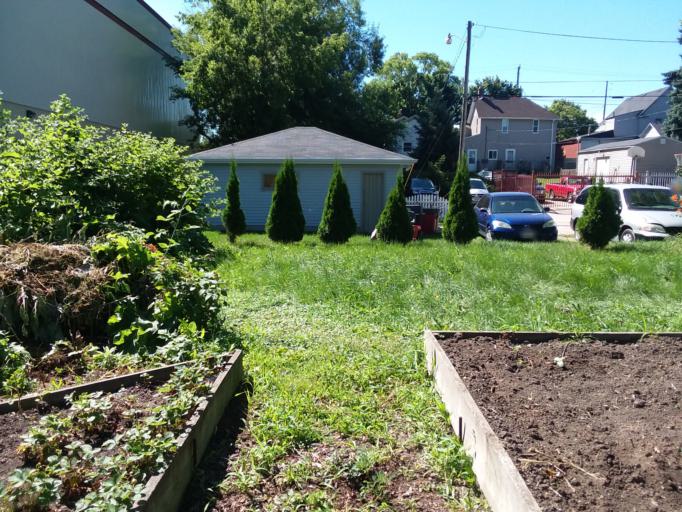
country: US
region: Wisconsin
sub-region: Milwaukee County
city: Saint Francis
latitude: 42.9986
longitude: -87.8952
